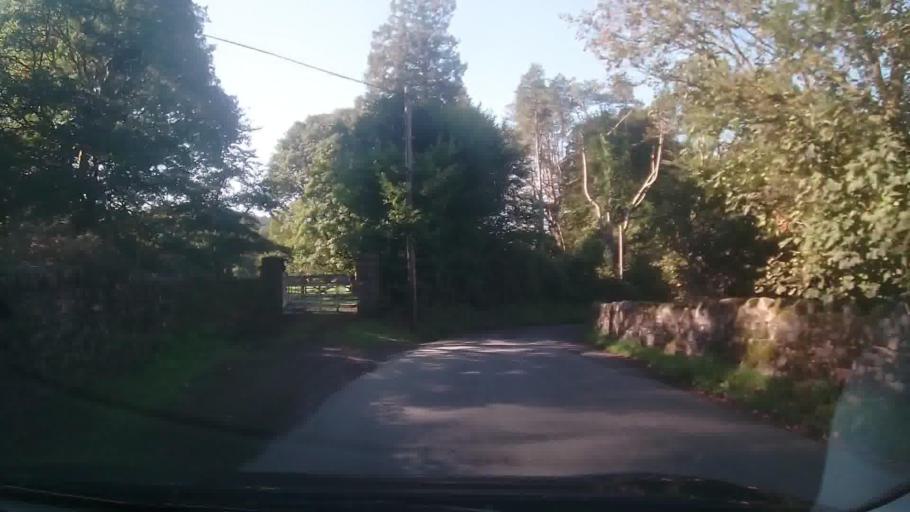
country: GB
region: England
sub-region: Cumbria
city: Millom
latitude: 54.3937
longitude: -3.2788
